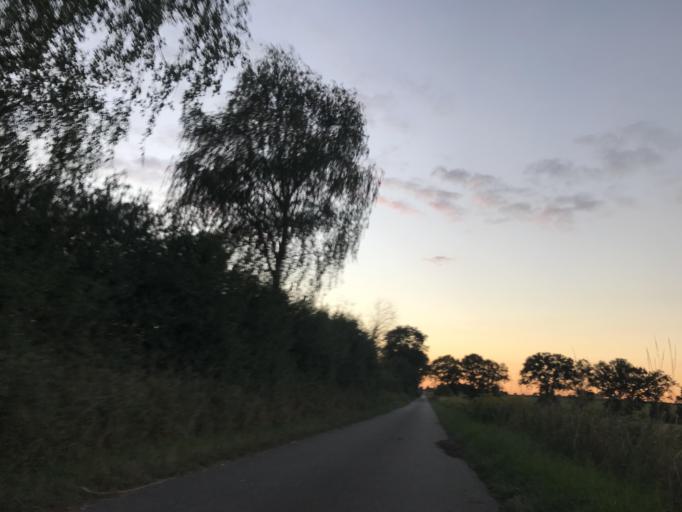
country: DE
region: Lower Saxony
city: Reinstorf
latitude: 53.2288
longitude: 10.5915
